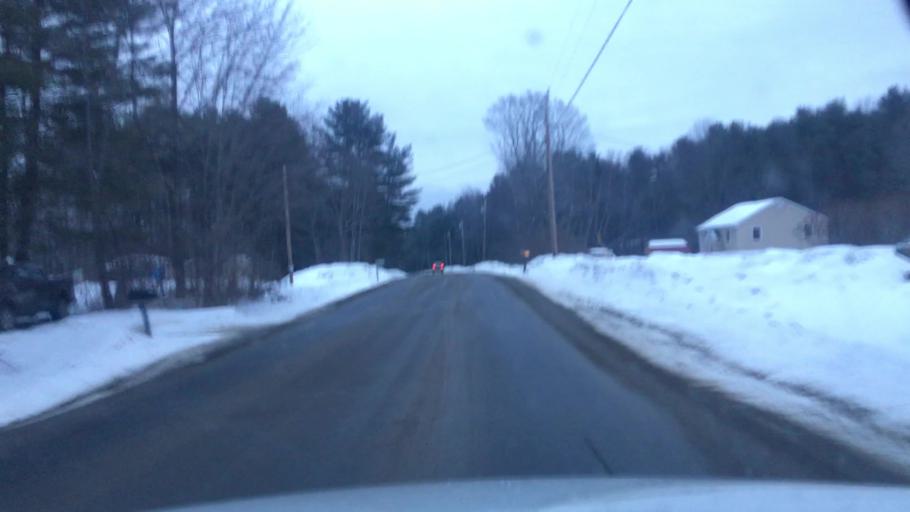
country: US
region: Maine
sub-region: Kennebec County
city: Oakland
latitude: 44.6252
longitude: -69.7287
